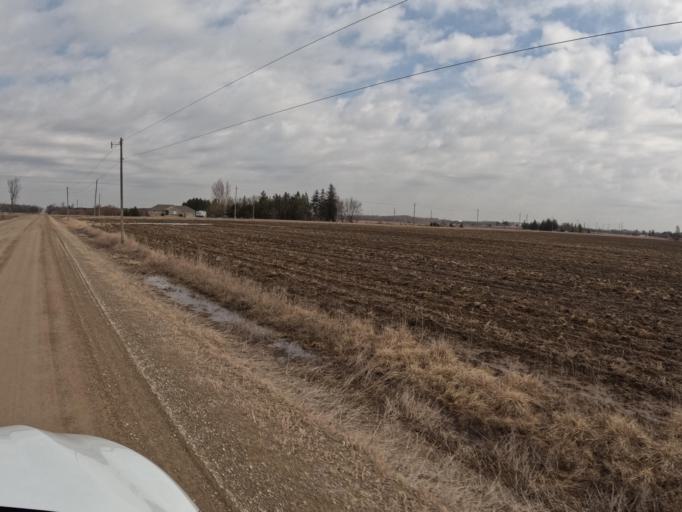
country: CA
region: Ontario
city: Orangeville
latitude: 43.9198
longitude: -80.2177
